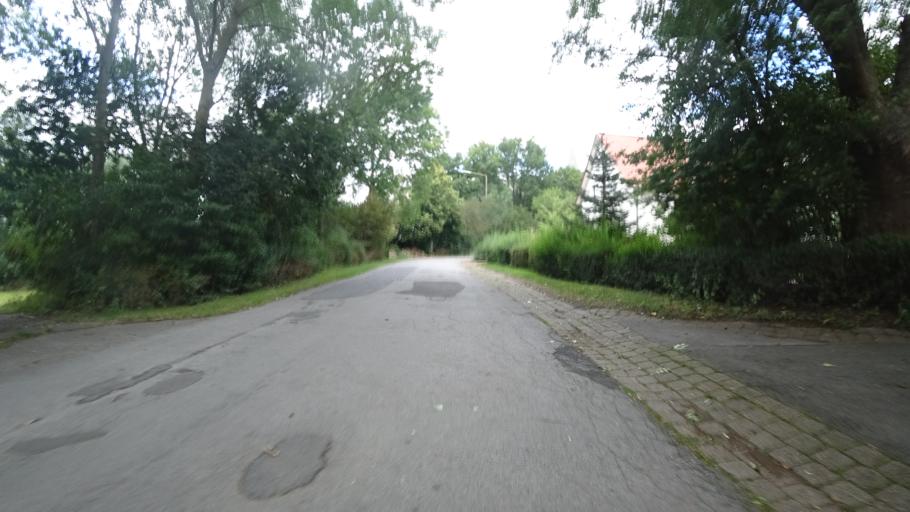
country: DE
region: Lower Saxony
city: Raddestorf
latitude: 52.4158
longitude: 9.0085
